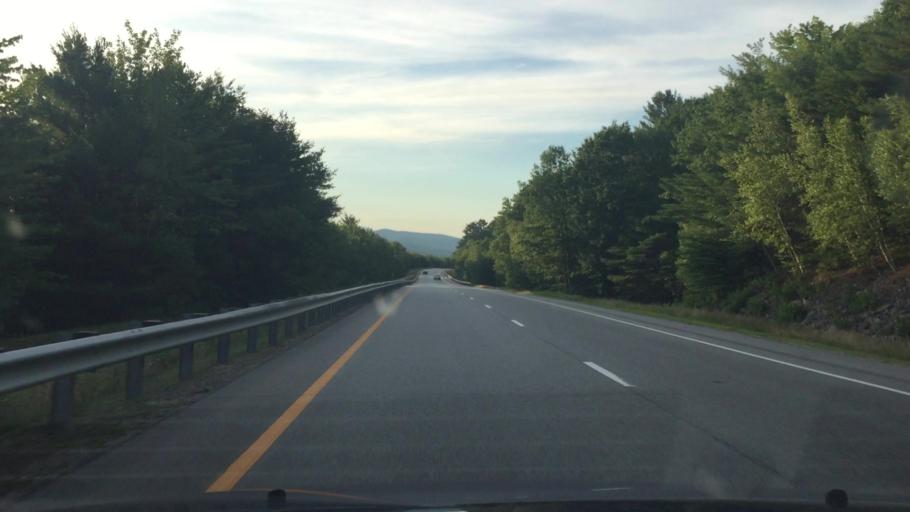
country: US
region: New Hampshire
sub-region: Grafton County
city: Ashland
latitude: 43.7195
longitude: -71.6535
